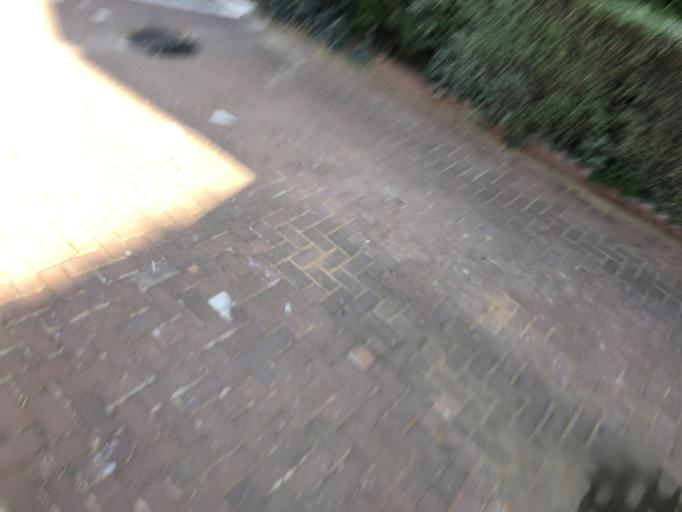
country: IL
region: Central District
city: Yehud
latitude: 32.0408
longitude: 34.8943
